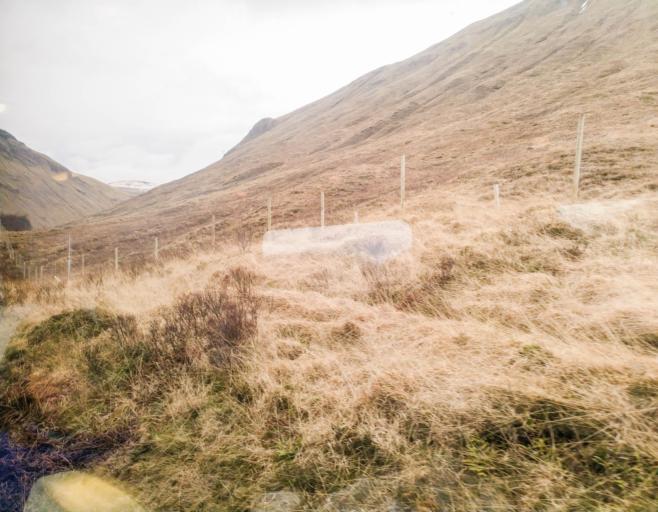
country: GB
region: Scotland
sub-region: Argyll and Bute
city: Garelochhead
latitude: 56.4806
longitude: -4.7100
